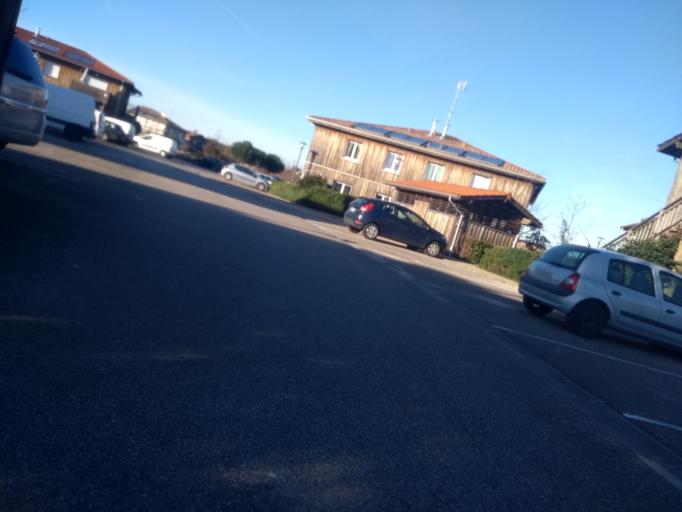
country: FR
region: Aquitaine
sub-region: Departement de la Gironde
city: Le Barp
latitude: 44.6069
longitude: -0.7816
